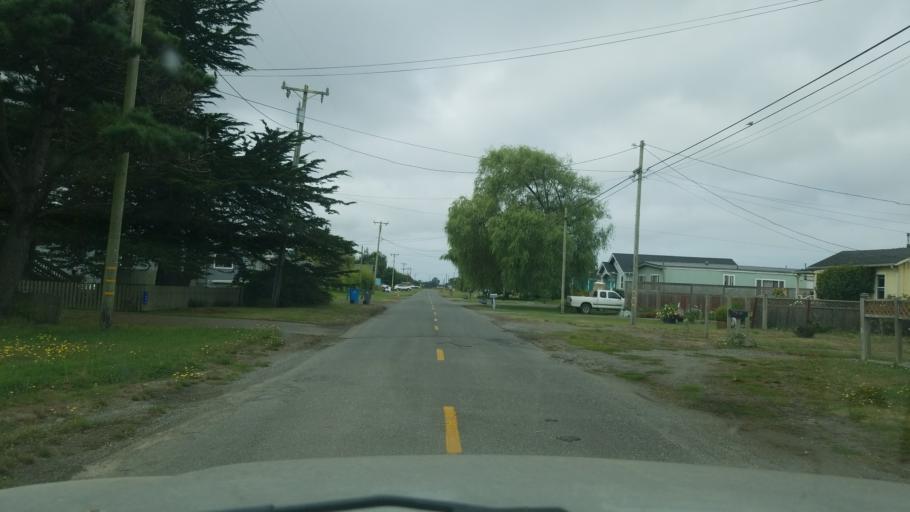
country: US
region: California
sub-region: Humboldt County
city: Ferndale
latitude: 40.5954
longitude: -124.2788
